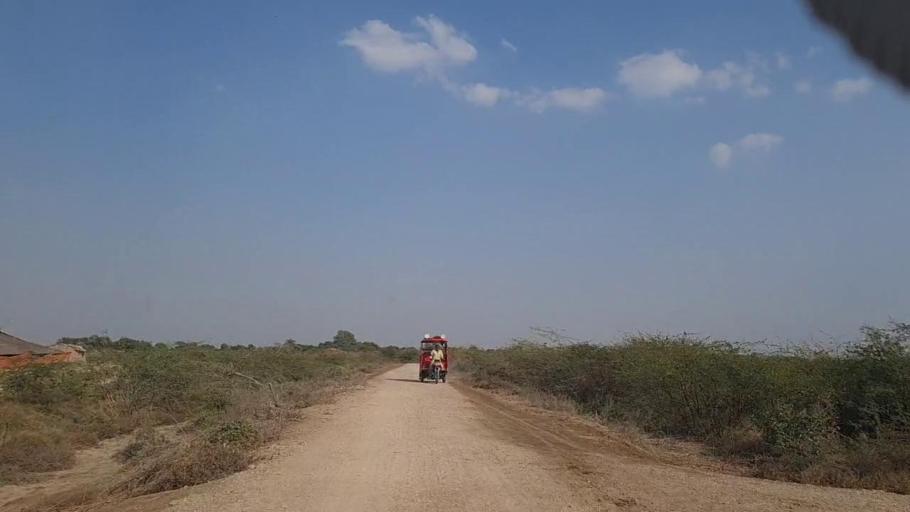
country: PK
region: Sindh
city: Jati
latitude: 24.4295
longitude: 68.3748
